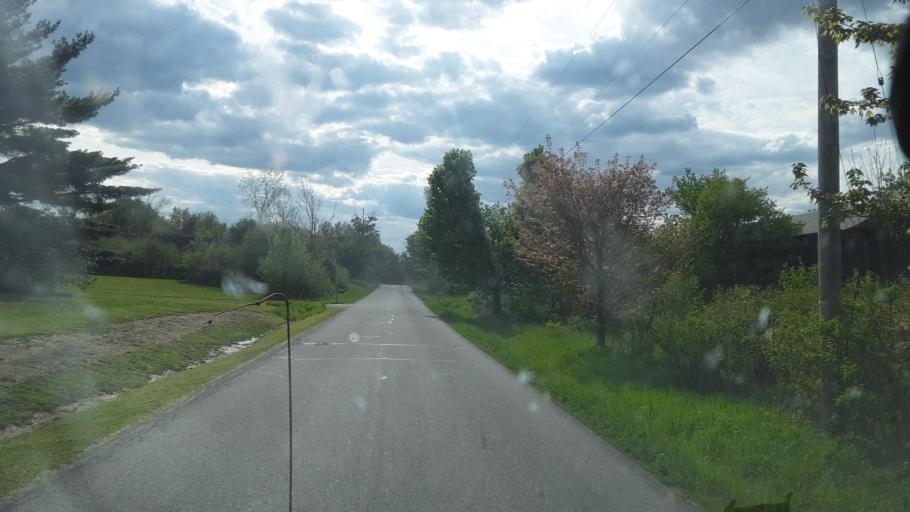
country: US
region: Ohio
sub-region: Portage County
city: Garrettsville
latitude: 41.3478
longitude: -81.0188
